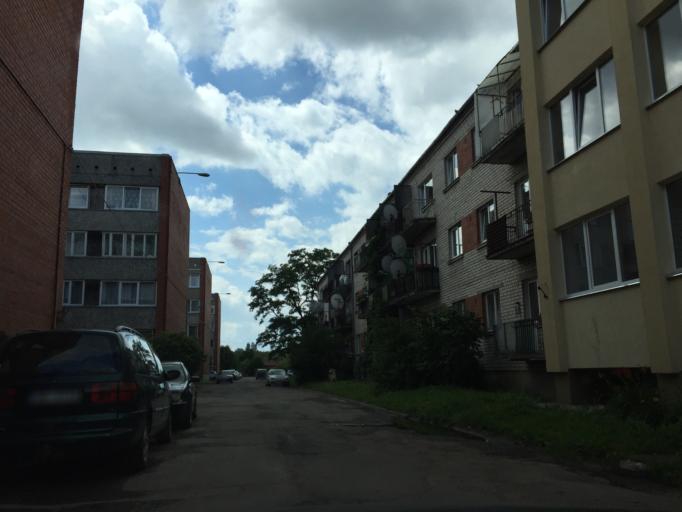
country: LV
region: Ozolnieku
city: Ozolnieki
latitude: 56.6576
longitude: 23.7590
